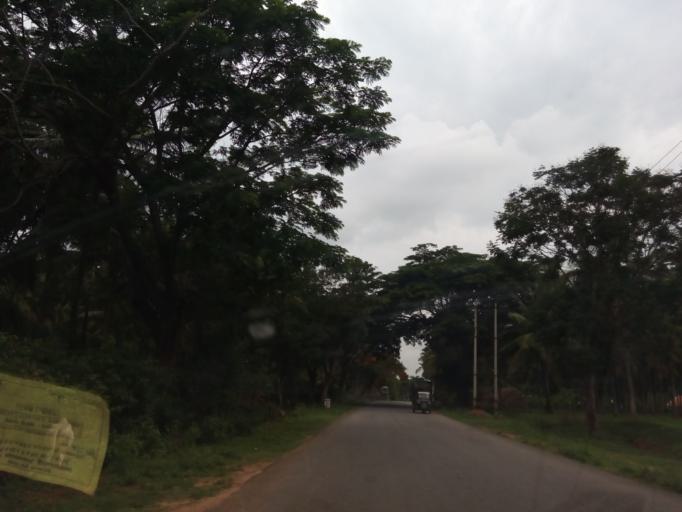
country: IN
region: Karnataka
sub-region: Hassan
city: Shravanabelagola
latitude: 12.8667
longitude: 76.4624
